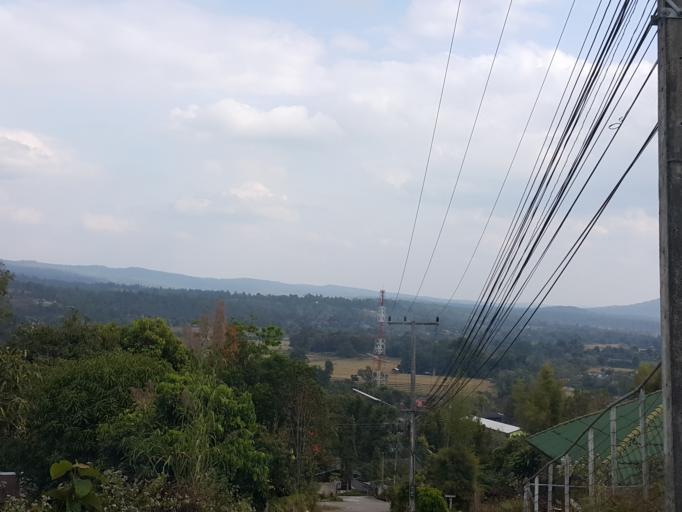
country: TH
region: Chiang Mai
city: Om Koi
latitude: 17.7992
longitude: 98.3538
